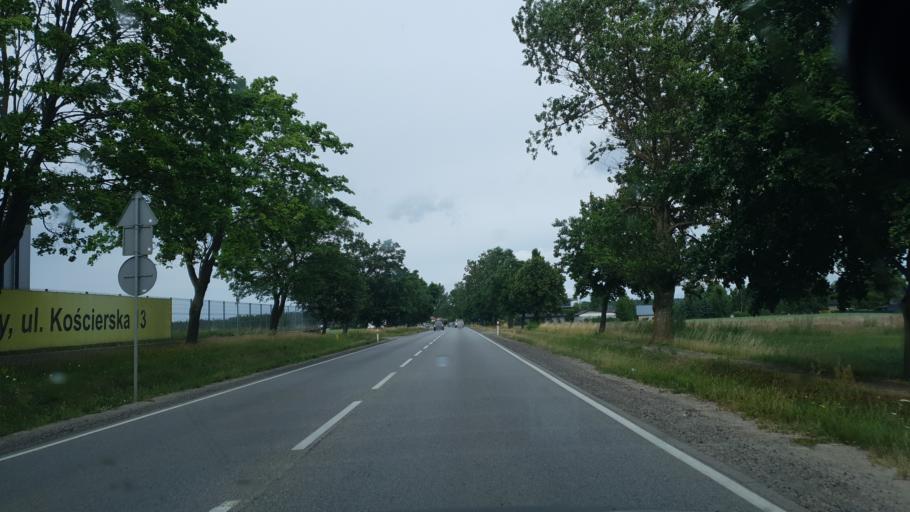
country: PL
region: Pomeranian Voivodeship
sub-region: Powiat kartuski
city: Banino
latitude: 54.4233
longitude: 18.3836
